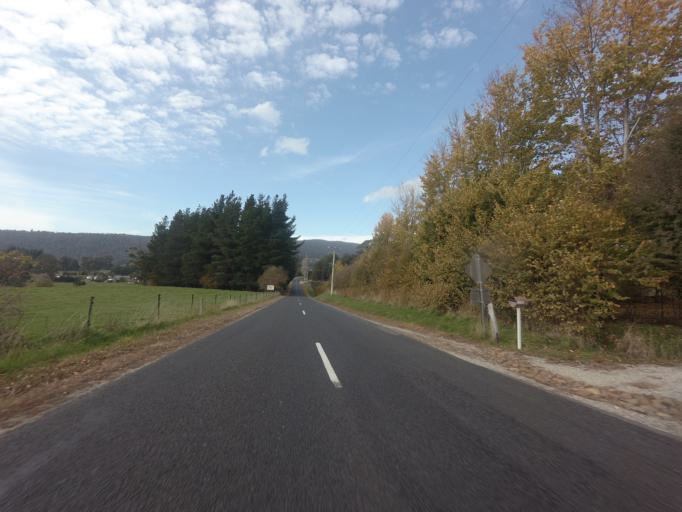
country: AU
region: Tasmania
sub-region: Meander Valley
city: Deloraine
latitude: -41.6279
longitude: 146.7060
